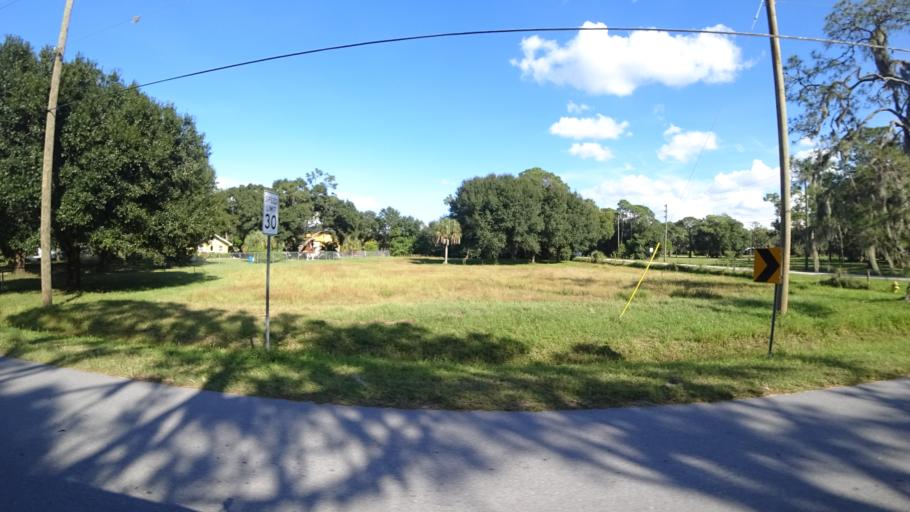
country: US
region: Florida
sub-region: Manatee County
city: Samoset
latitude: 27.4640
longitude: -82.4741
